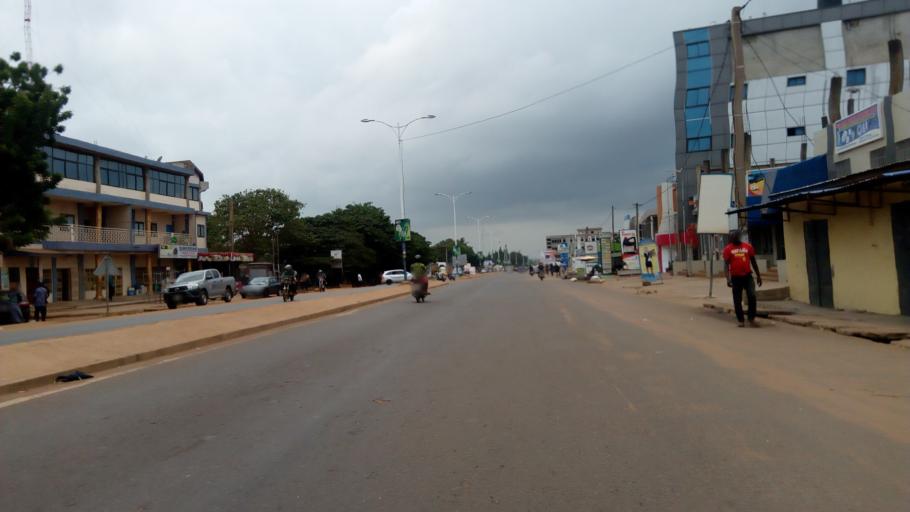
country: TG
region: Maritime
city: Lome
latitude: 6.2302
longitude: 1.2108
